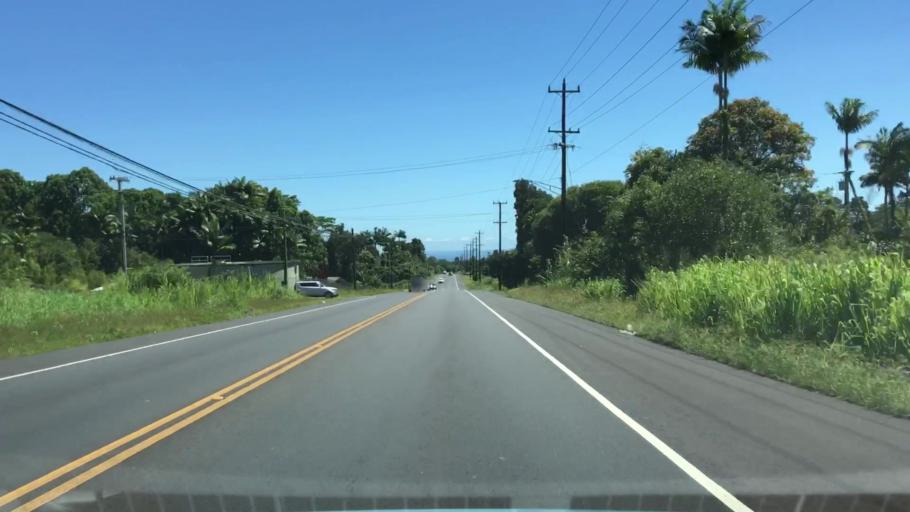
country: US
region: Hawaii
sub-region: Hawaii County
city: Mountain View
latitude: 19.5669
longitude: -155.0847
